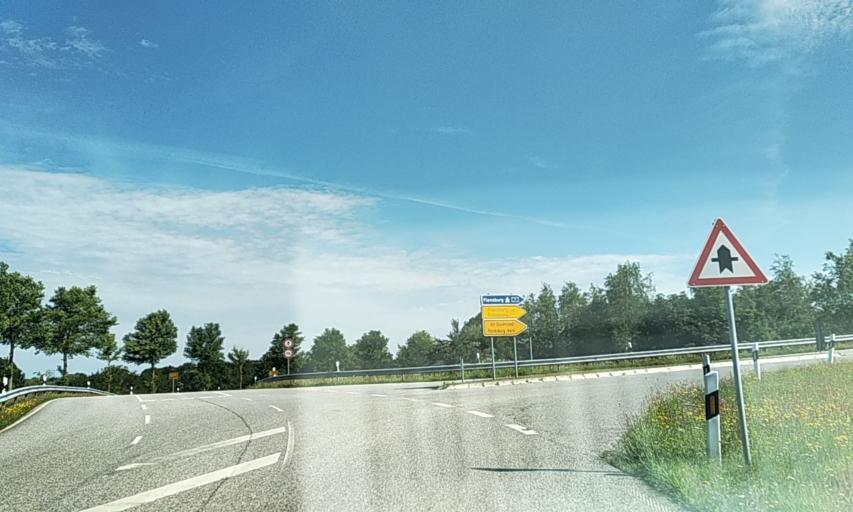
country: DE
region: Schleswig-Holstein
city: Fockbek
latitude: 54.3295
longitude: 9.6196
